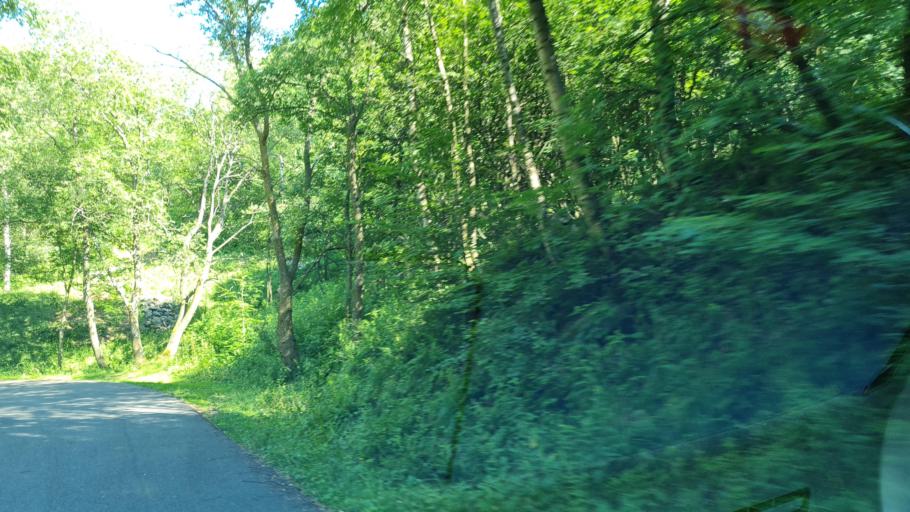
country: IT
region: Piedmont
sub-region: Provincia di Torino
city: Quincinetto
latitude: 45.5487
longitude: 7.7739
